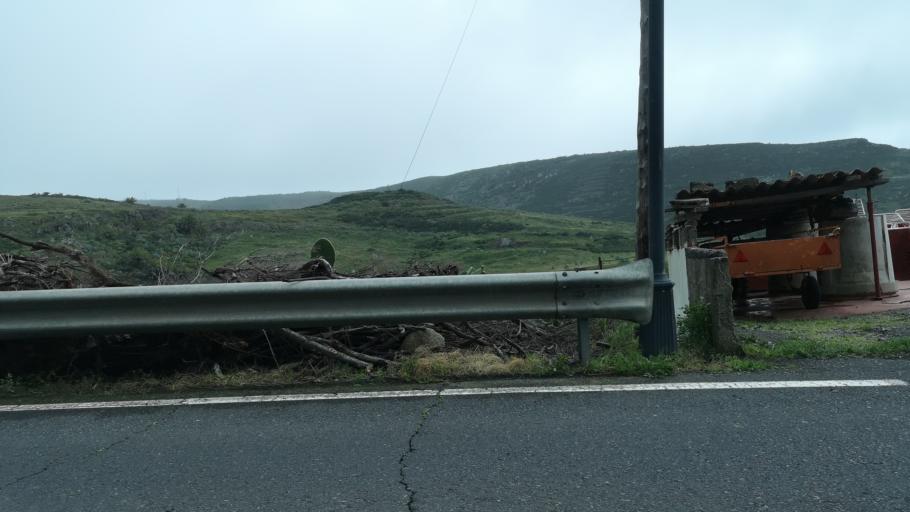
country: ES
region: Canary Islands
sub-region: Provincia de Santa Cruz de Tenerife
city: Vallehermosa
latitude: 28.1362
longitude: -17.3165
